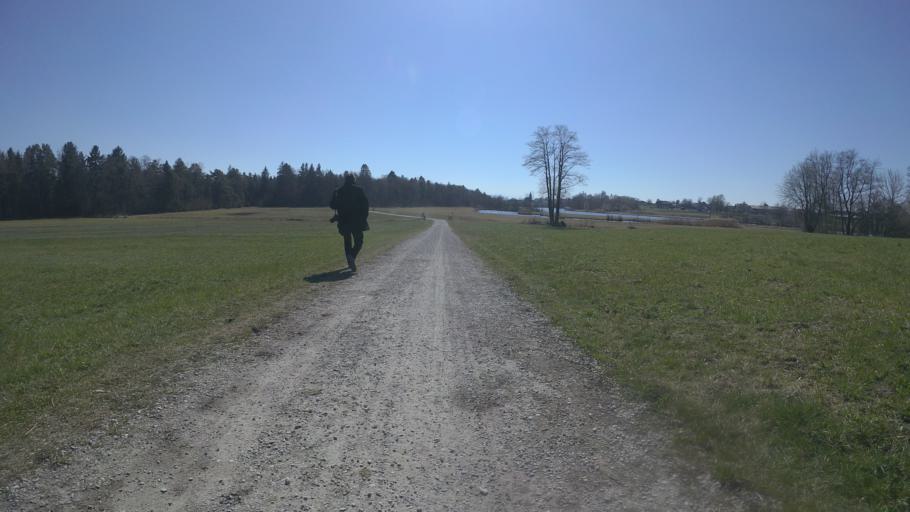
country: DE
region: Bavaria
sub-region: Upper Bavaria
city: Seeon-Seebruck
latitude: 47.9407
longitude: 12.4931
